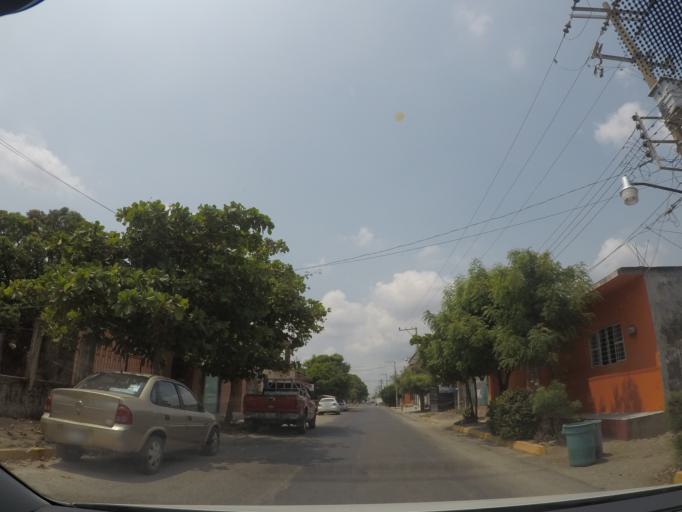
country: MX
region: Oaxaca
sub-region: El Espinal
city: El Espinal
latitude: 16.4900
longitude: -95.0439
